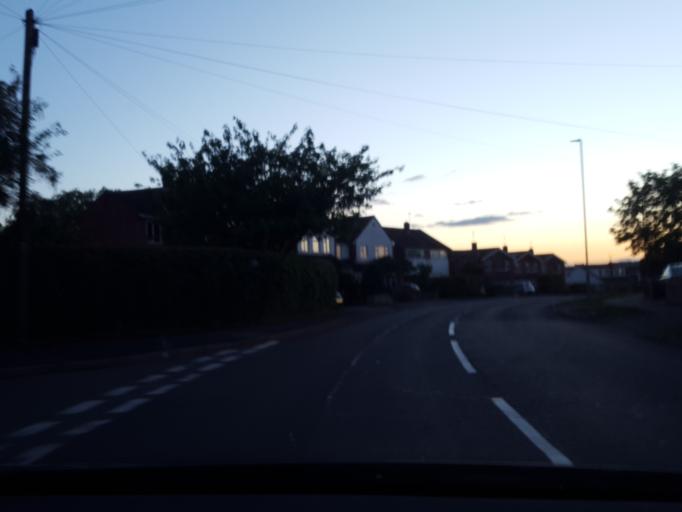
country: GB
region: England
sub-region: Leicestershire
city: Loughborough
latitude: 52.7521
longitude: -1.2194
